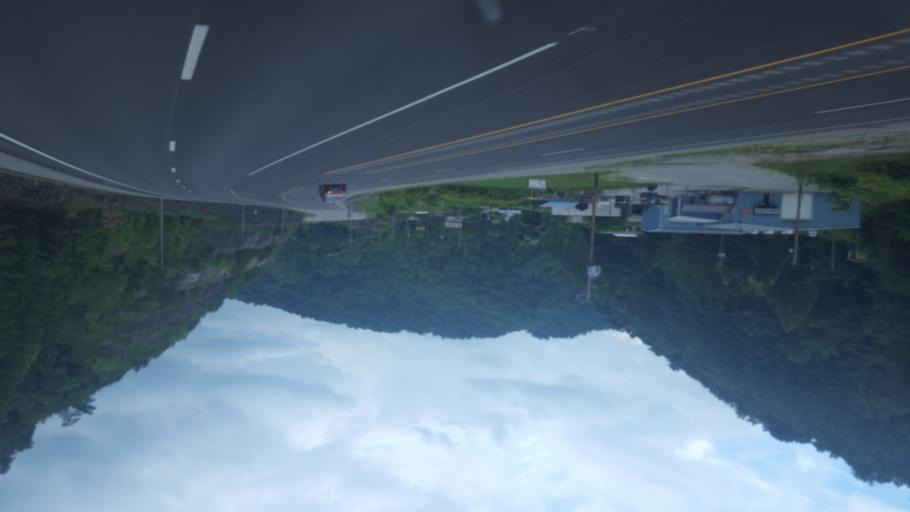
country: US
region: Kentucky
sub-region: Letcher County
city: Jenkins
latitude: 37.2819
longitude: -82.5740
